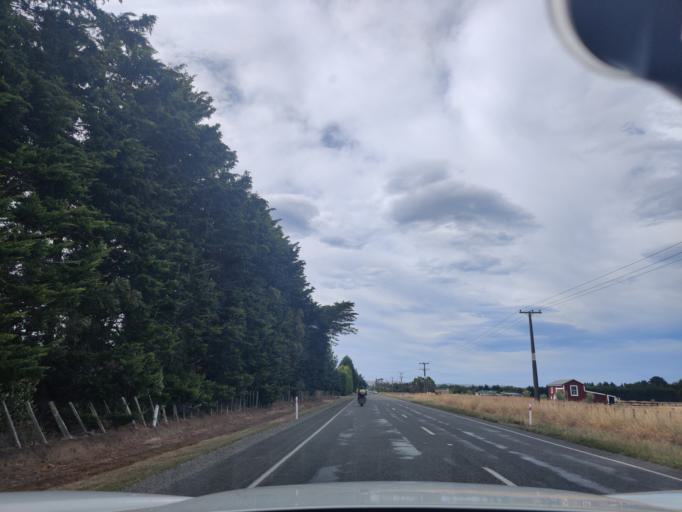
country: NZ
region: Wellington
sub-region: Masterton District
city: Masterton
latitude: -40.9054
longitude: 175.6650
